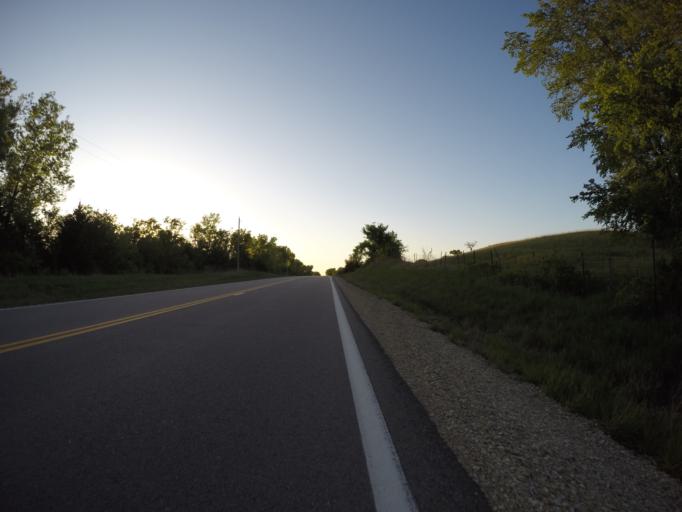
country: US
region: Kansas
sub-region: Riley County
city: Ogden
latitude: 39.2366
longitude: -96.7595
